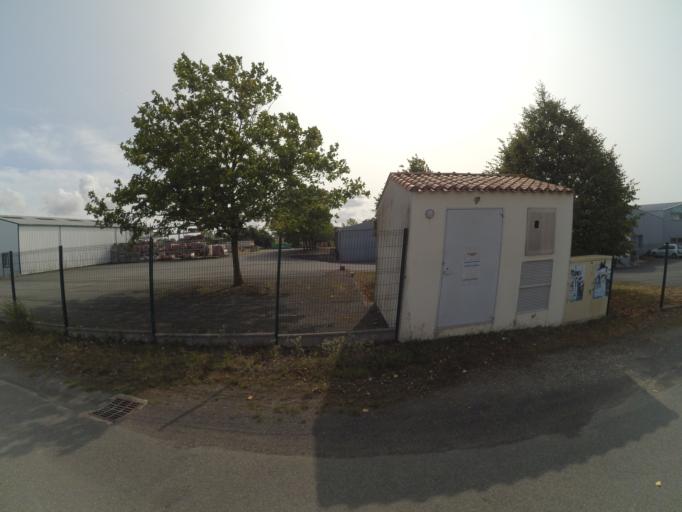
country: FR
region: Pays de la Loire
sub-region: Departement de la Vendee
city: Treize-Septiers
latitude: 46.9808
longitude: -1.2243
